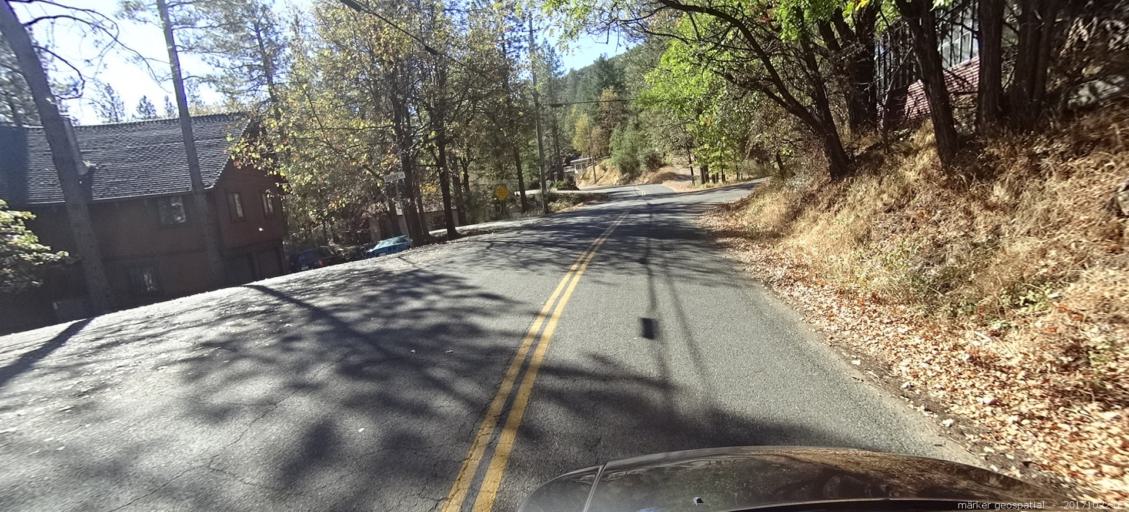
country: US
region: California
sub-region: Shasta County
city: Central Valley (historical)
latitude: 40.8591
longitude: -122.3968
